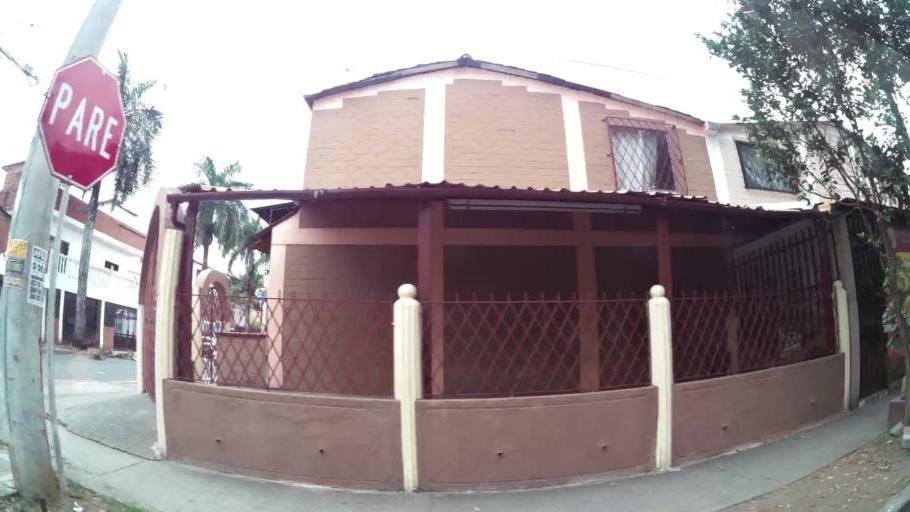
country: CO
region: Valle del Cauca
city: Cali
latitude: 3.4661
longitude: -76.4948
